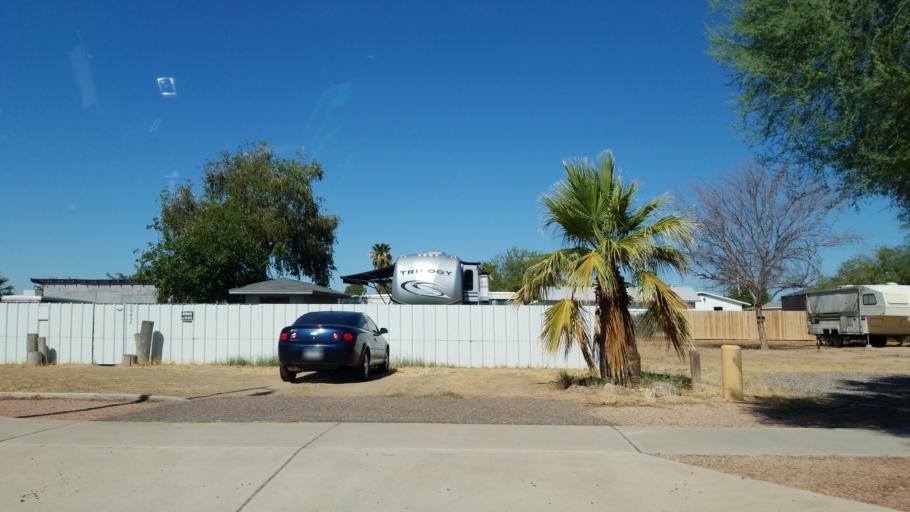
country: US
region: Arizona
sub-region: Maricopa County
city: Peoria
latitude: 33.6742
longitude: -112.1348
